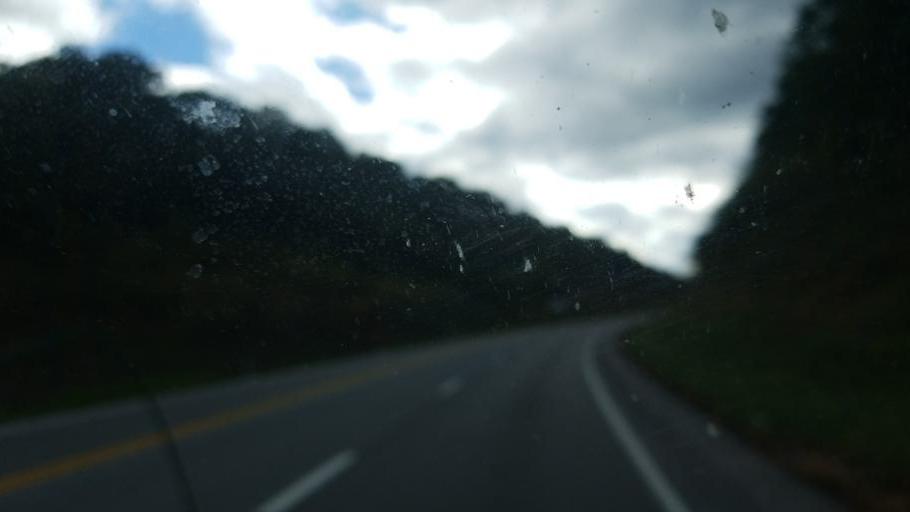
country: US
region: Pennsylvania
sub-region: Fulton County
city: McConnellsburg
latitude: 39.9443
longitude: -77.9704
